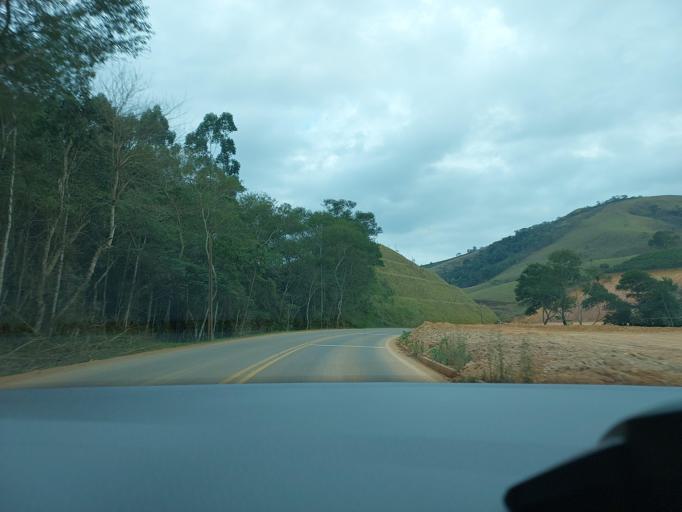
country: BR
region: Minas Gerais
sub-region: Mirai
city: Mirai
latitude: -20.9850
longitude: -42.5800
